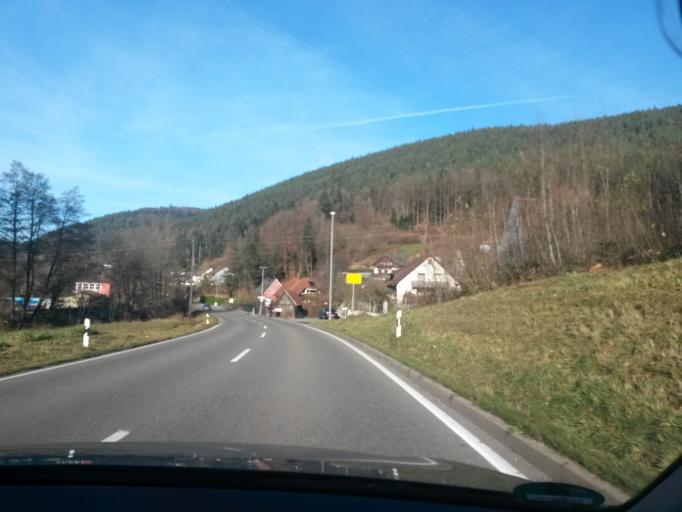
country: DE
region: Baden-Wuerttemberg
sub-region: Karlsruhe Region
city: Hofen an der Enz
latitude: 48.7614
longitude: 8.5877
